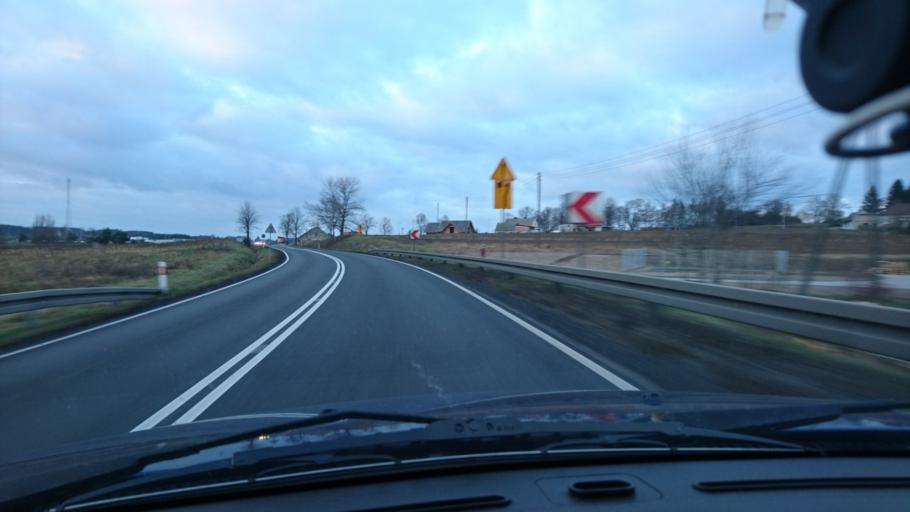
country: PL
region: Greater Poland Voivodeship
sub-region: Powiat ostrzeszowski
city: Ostrzeszow
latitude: 51.3848
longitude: 17.9496
